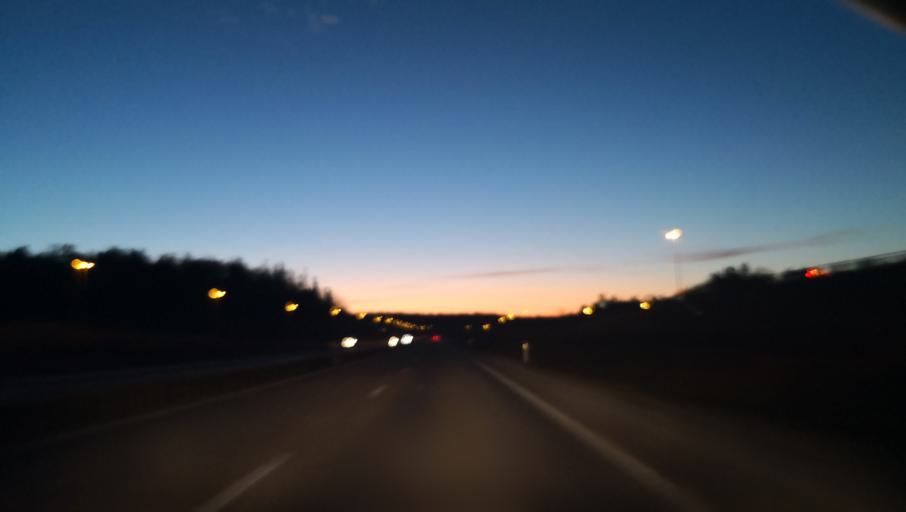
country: SE
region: Stockholm
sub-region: Nynashamns Kommun
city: Osmo
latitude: 58.9435
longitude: 17.9137
